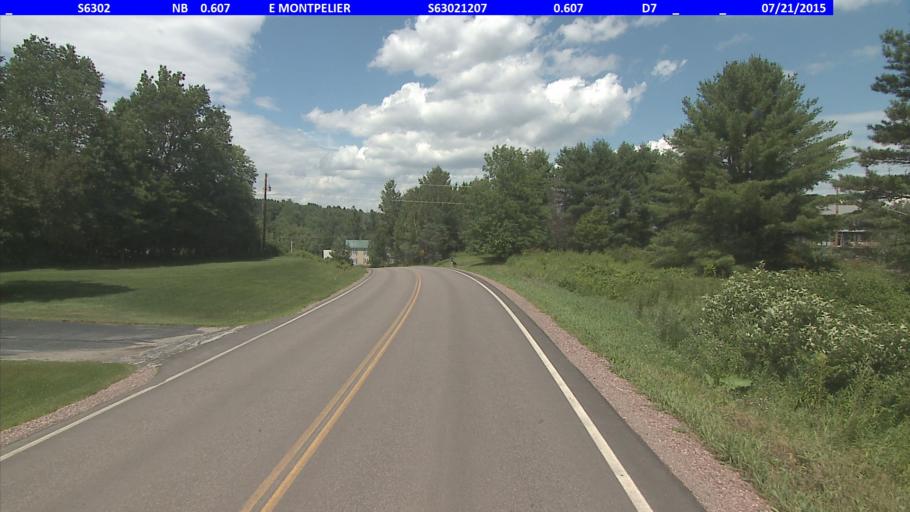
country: US
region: Vermont
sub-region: Washington County
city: Montpelier
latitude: 44.2521
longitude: -72.5214
